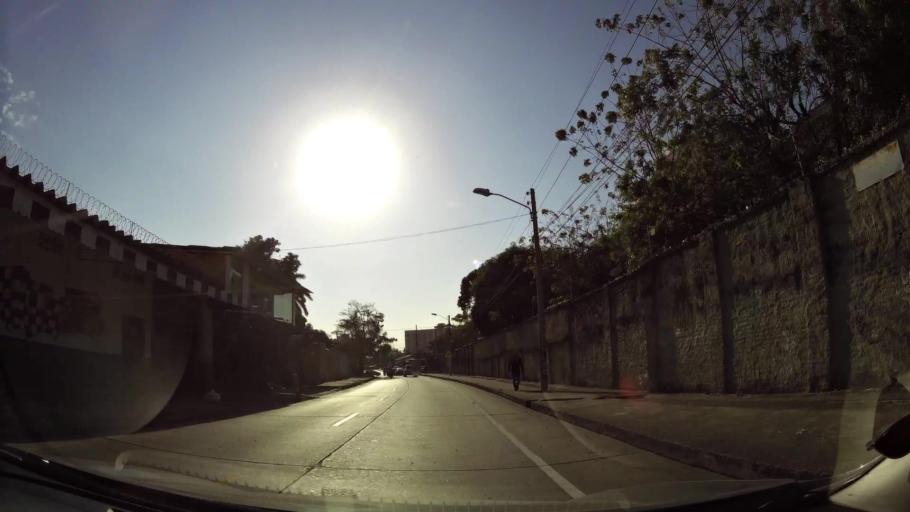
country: CO
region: Atlantico
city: Barranquilla
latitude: 10.9965
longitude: -74.8027
